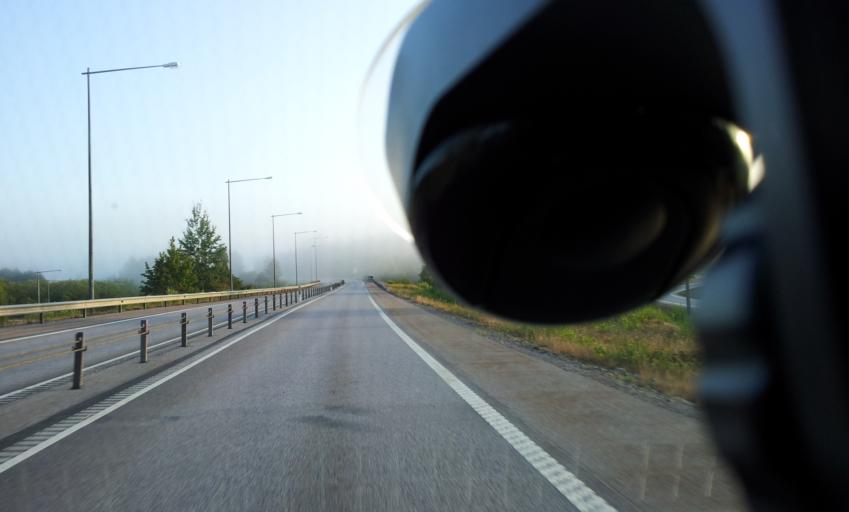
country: SE
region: Kalmar
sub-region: Vasterviks Kommun
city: Vaestervik
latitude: 57.7617
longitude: 16.5567
